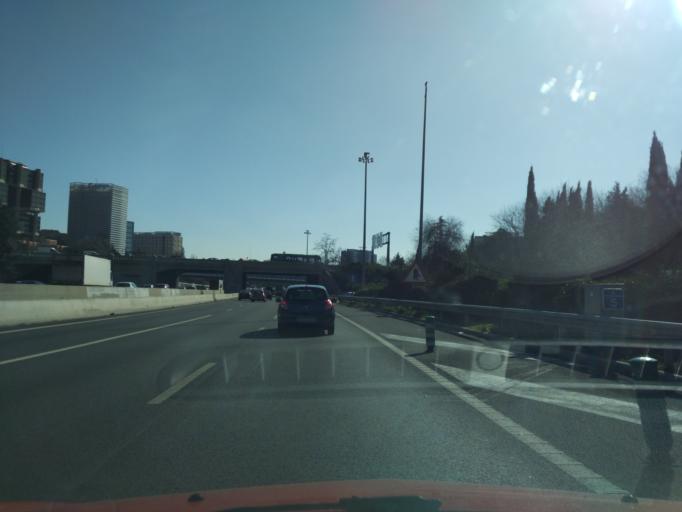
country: ES
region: Madrid
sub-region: Provincia de Madrid
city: Ciudad Lineal
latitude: 40.4458
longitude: -3.6617
